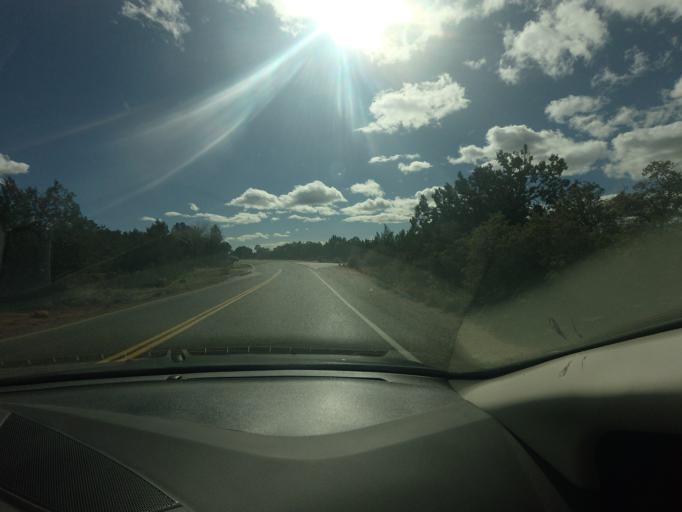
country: US
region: Arizona
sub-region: Yavapai County
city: West Sedona
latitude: 34.8808
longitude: -111.8207
